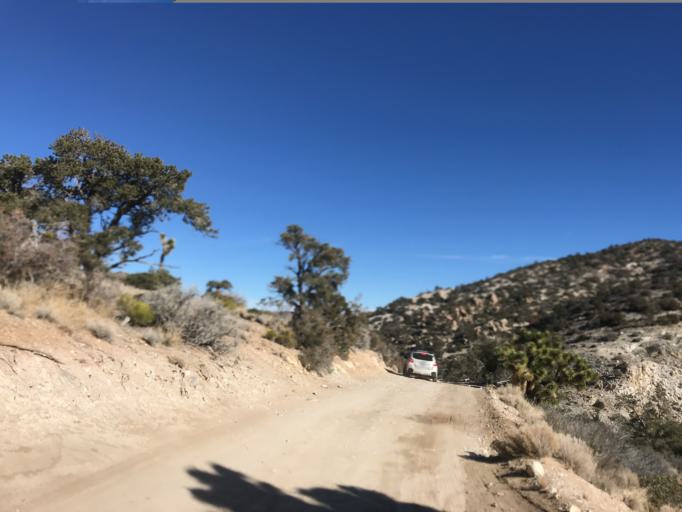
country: US
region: California
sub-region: San Bernardino County
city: Big Bear City
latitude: 34.2282
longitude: -116.6653
